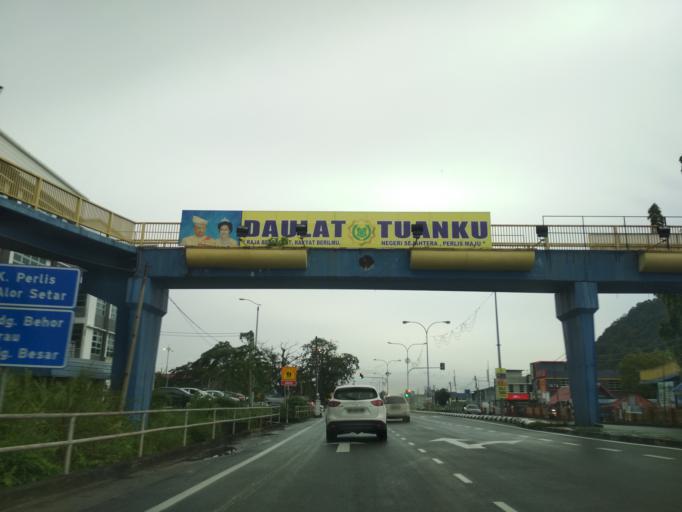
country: MY
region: Perlis
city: Kangar
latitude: 6.4339
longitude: 100.1953
